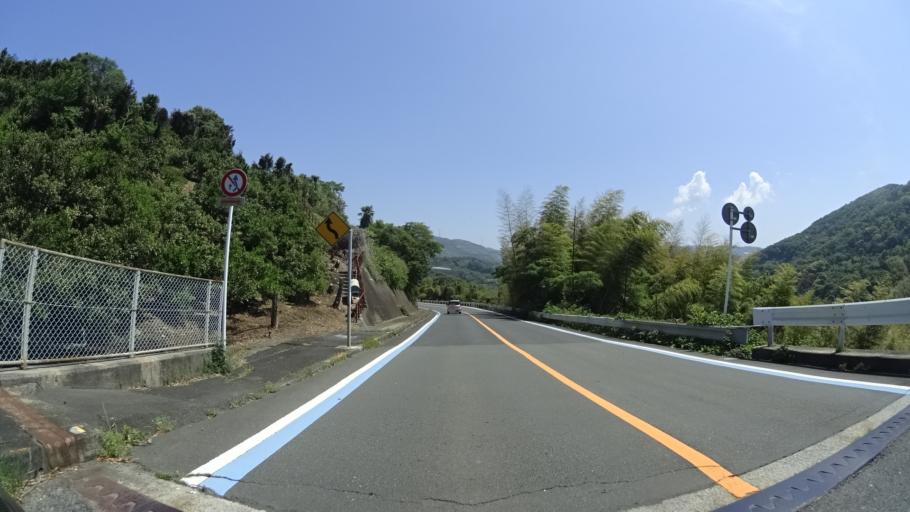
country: JP
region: Ehime
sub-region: Nishiuwa-gun
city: Ikata-cho
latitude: 33.4827
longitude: 132.3336
